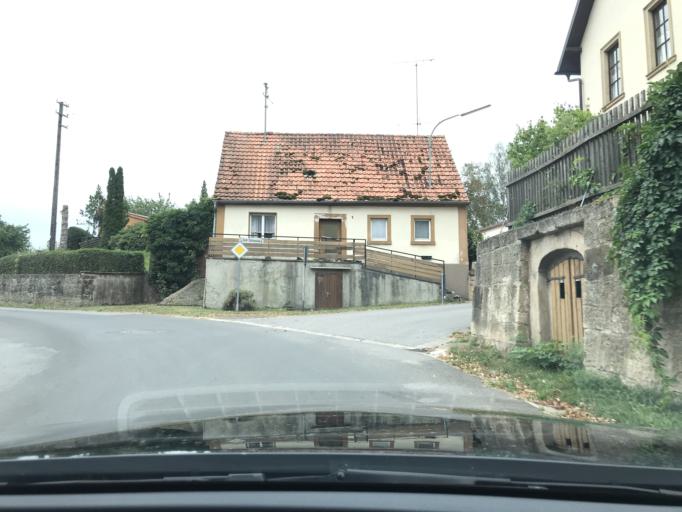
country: DE
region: Bavaria
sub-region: Regierungsbezirk Unterfranken
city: Burgpreppach
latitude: 50.1175
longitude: 10.6721
